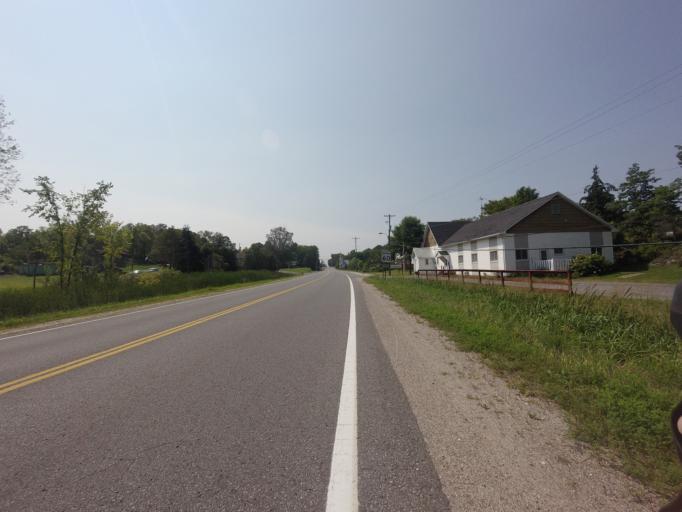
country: CA
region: Ontario
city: Skatepark
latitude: 44.6568
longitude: -76.7118
